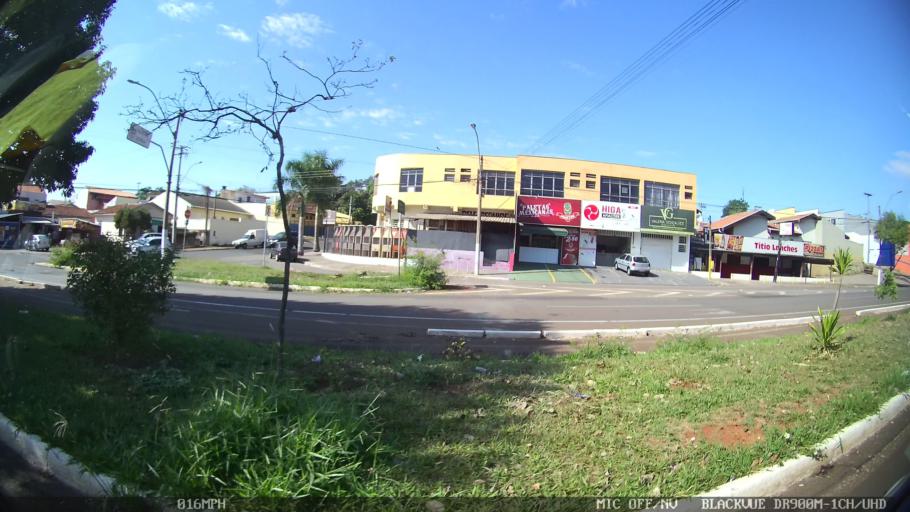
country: BR
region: Sao Paulo
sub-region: Americana
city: Americana
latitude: -22.7585
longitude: -47.3309
